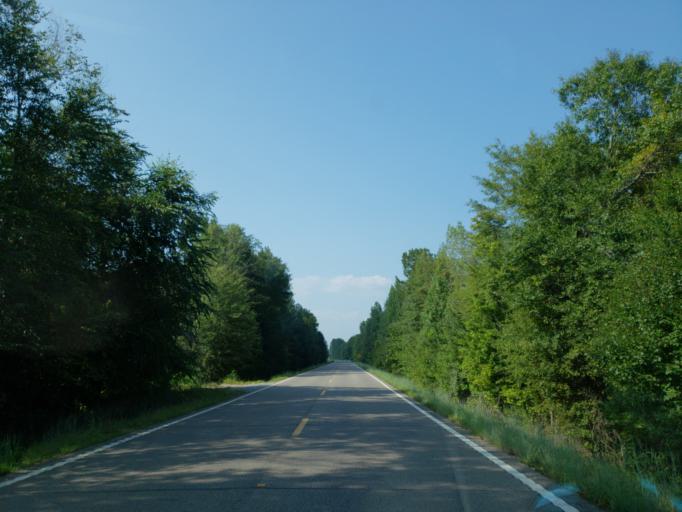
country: US
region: Mississippi
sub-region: Lauderdale County
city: Meridian
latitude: 32.2578
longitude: -88.7696
